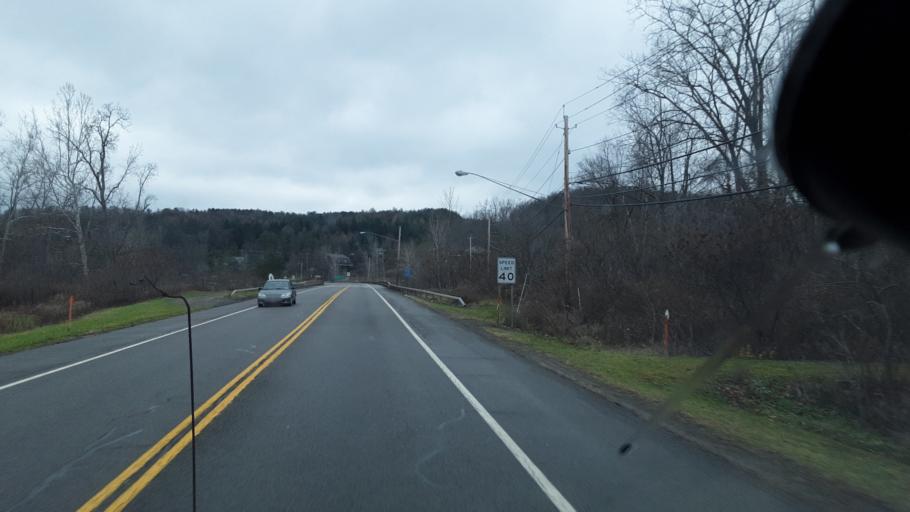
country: US
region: New York
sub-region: Allegany County
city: Houghton
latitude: 42.3844
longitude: -78.1544
